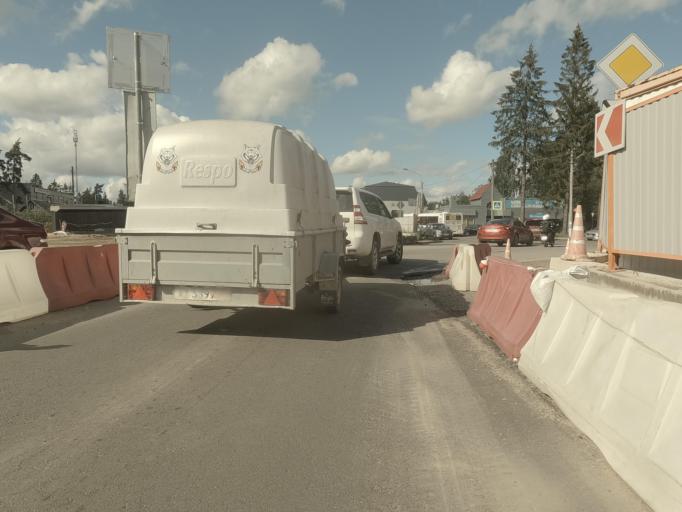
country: RU
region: Leningrad
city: Vsevolozhsk
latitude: 60.0135
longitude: 30.6663
